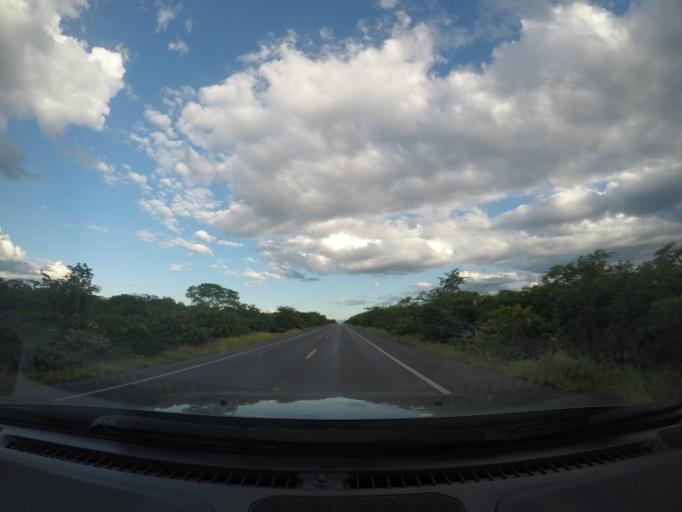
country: BR
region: Bahia
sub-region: Oliveira Dos Brejinhos
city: Beira Rio
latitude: -12.2782
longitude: -42.6943
